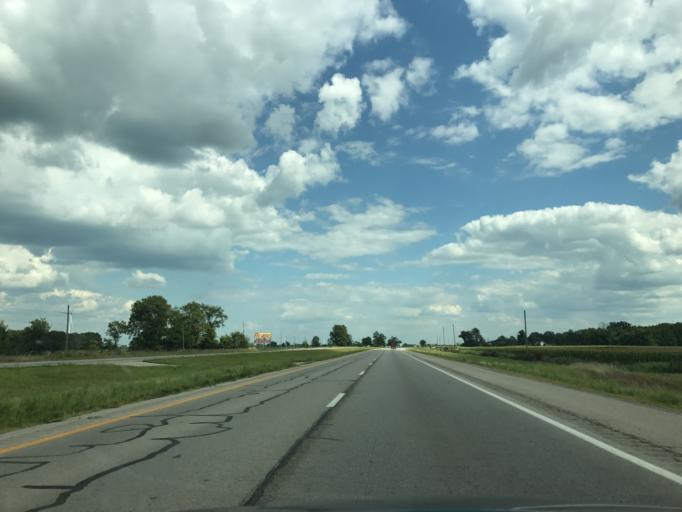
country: US
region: Indiana
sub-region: Allen County
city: Monroeville
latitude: 40.9933
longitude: -84.7914
